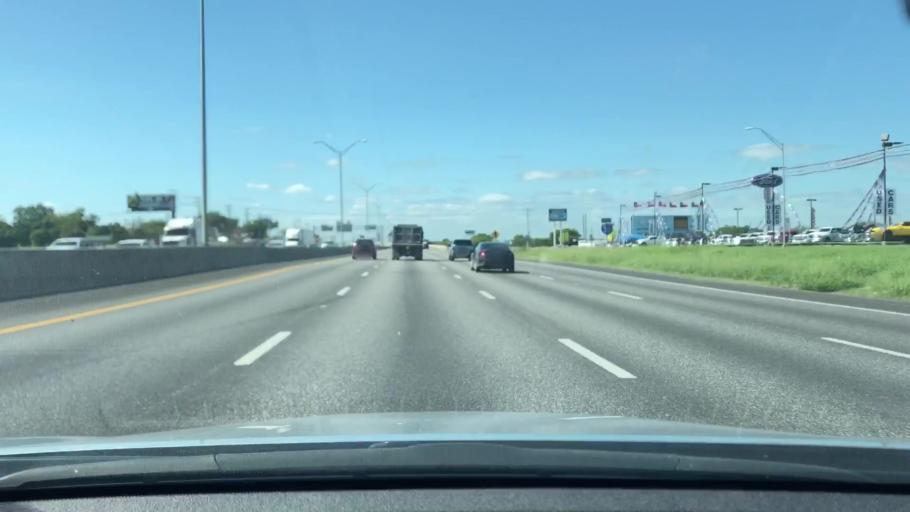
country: US
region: Texas
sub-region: Comal County
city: New Braunfels
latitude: 29.6847
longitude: -98.1341
